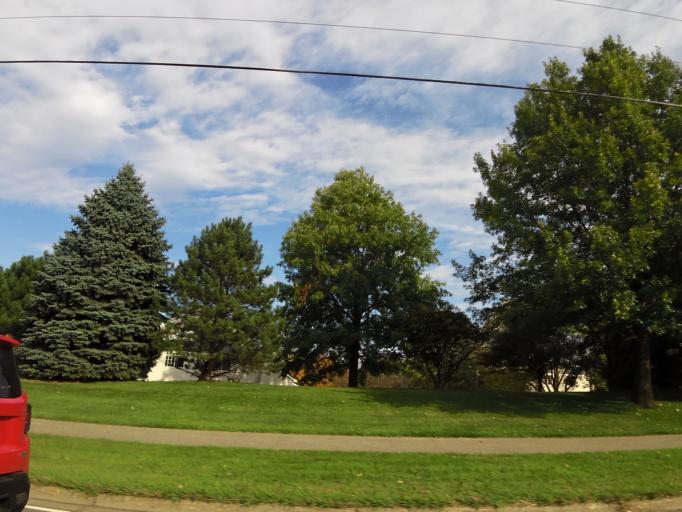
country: US
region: Minnesota
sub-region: Dakota County
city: Eagan
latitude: 44.8047
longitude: -93.2041
